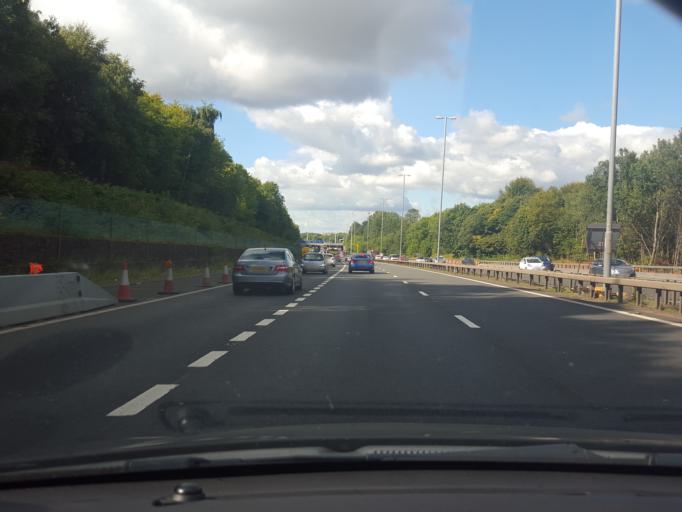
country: GB
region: Scotland
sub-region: South Lanarkshire
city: Uddingston
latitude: 55.8263
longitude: -4.0821
